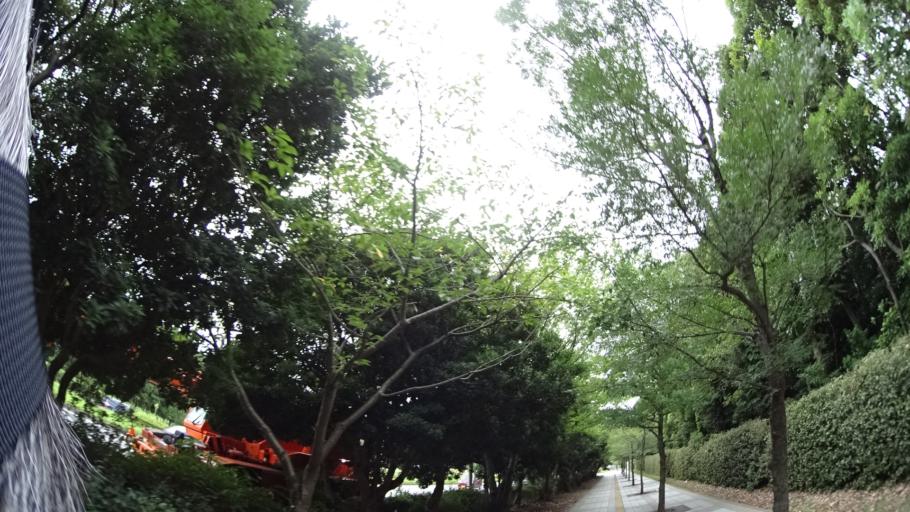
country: JP
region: Chiba
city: Funabashi
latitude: 35.6461
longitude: 140.0335
